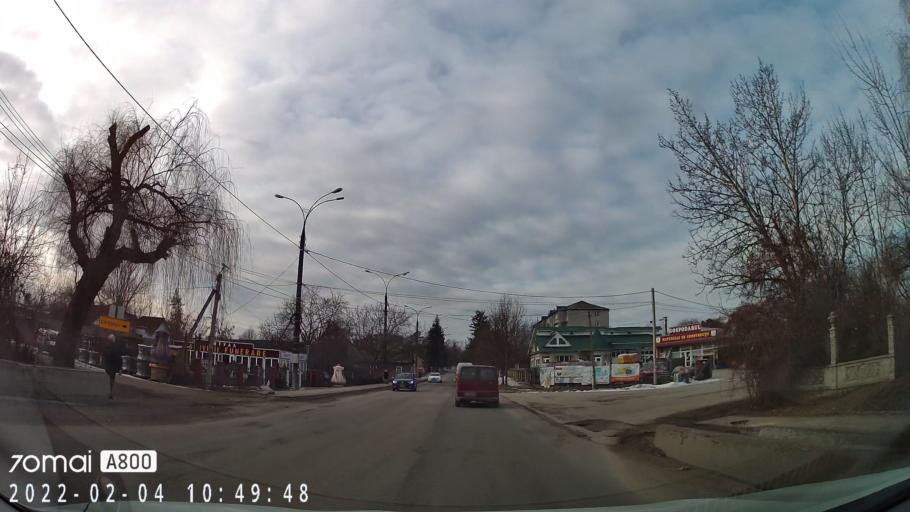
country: MD
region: Briceni
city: Briceni
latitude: 48.3570
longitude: 27.0894
